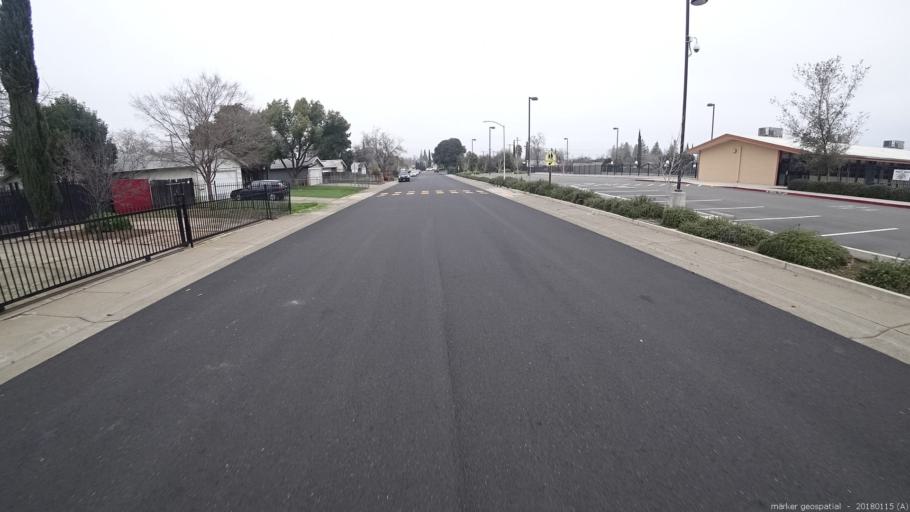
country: US
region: California
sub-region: Sacramento County
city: Rancho Cordova
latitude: 38.5867
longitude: -121.3009
